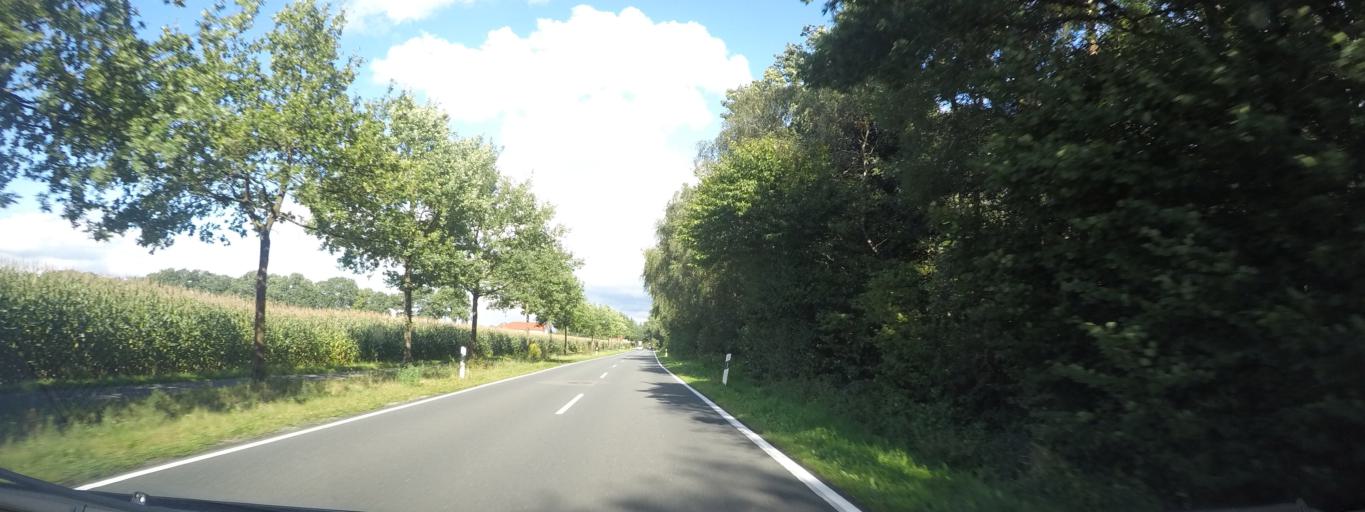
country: DE
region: North Rhine-Westphalia
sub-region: Regierungsbezirk Arnsberg
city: Lippstadt
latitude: 51.6977
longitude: 8.3170
